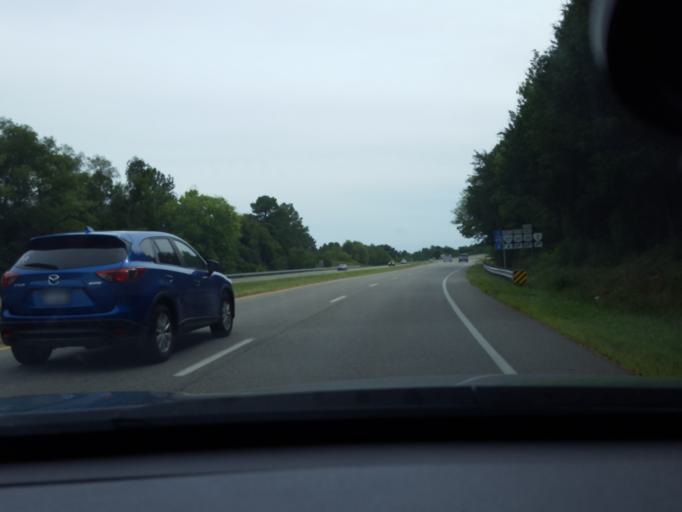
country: US
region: Virginia
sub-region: Caroline County
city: Bowling Green
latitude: 38.0475
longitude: -77.3402
